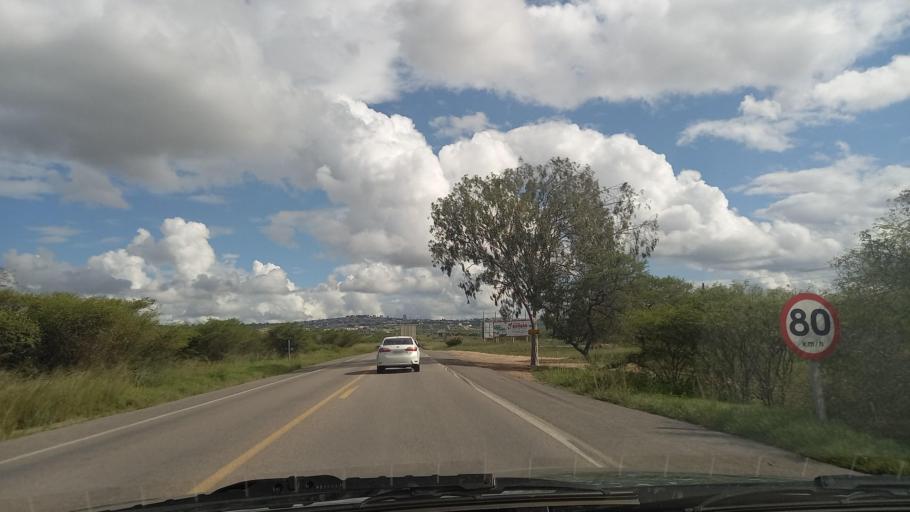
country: BR
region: Pernambuco
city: Garanhuns
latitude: -8.8347
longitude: -36.4547
